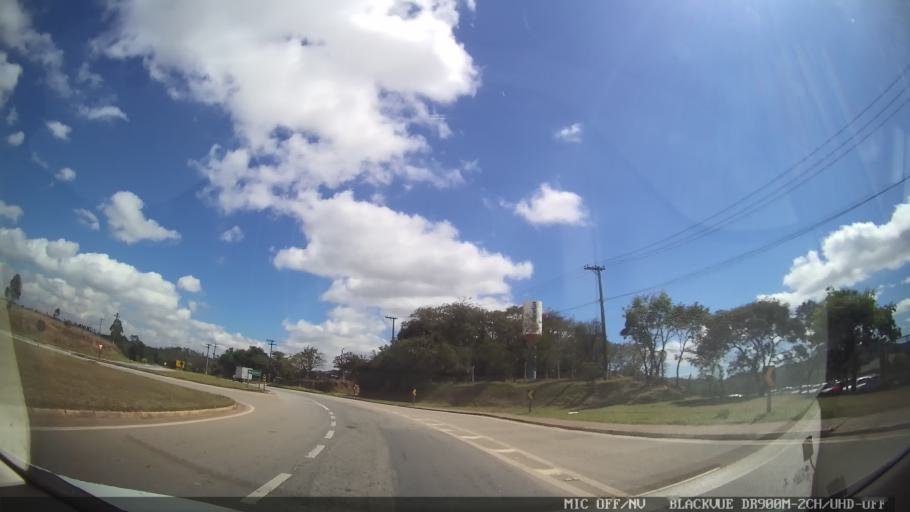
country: BR
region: Sao Paulo
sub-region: Francisco Morato
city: Francisco Morato
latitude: -23.2947
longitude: -46.7671
